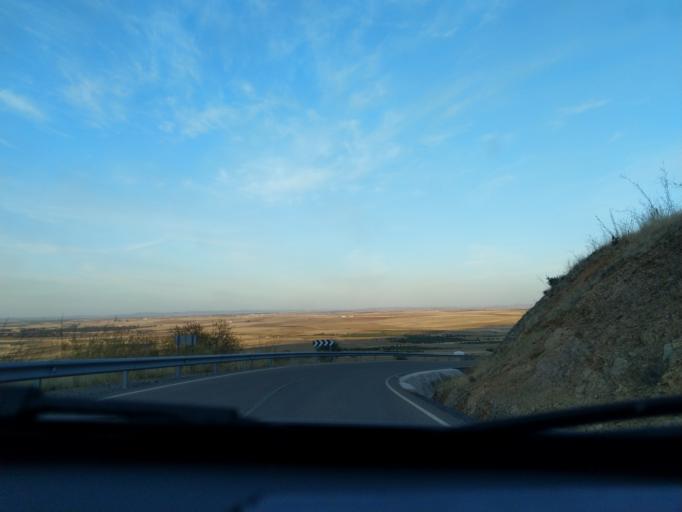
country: ES
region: Extremadura
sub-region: Provincia de Badajoz
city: Reina
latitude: 38.1892
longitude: -5.9480
